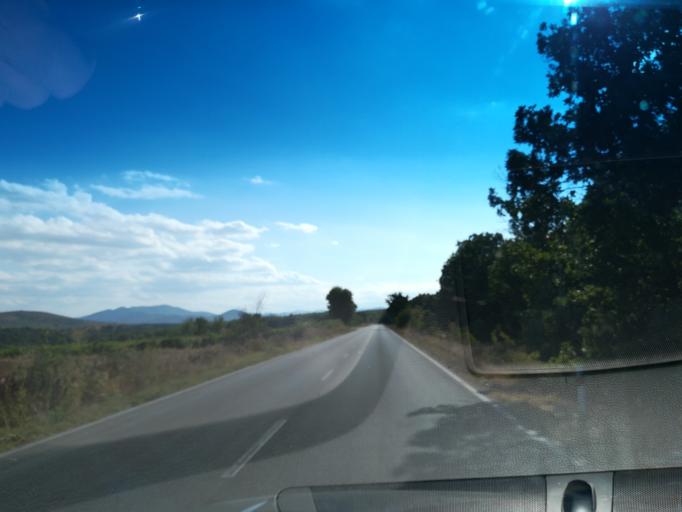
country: BG
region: Khaskovo
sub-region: Obshtina Mineralni Bani
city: Mineralni Bani
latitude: 42.0007
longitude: 25.3703
